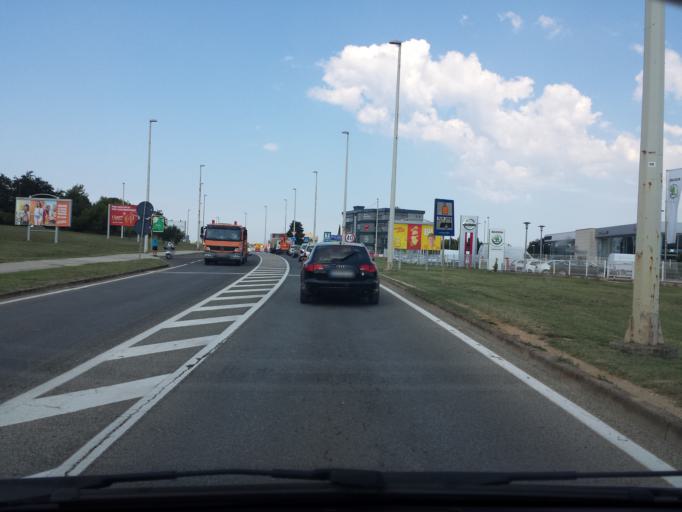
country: HR
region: Istarska
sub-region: Grad Pula
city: Pula
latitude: 44.8855
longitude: 13.8589
